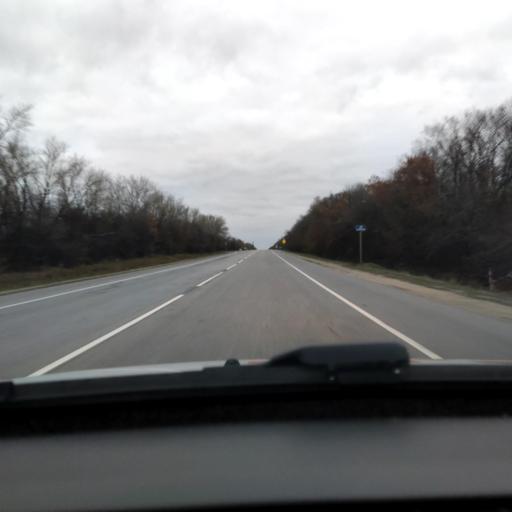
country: RU
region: Lipetsk
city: Khlevnoye
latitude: 52.3450
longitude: 39.1878
